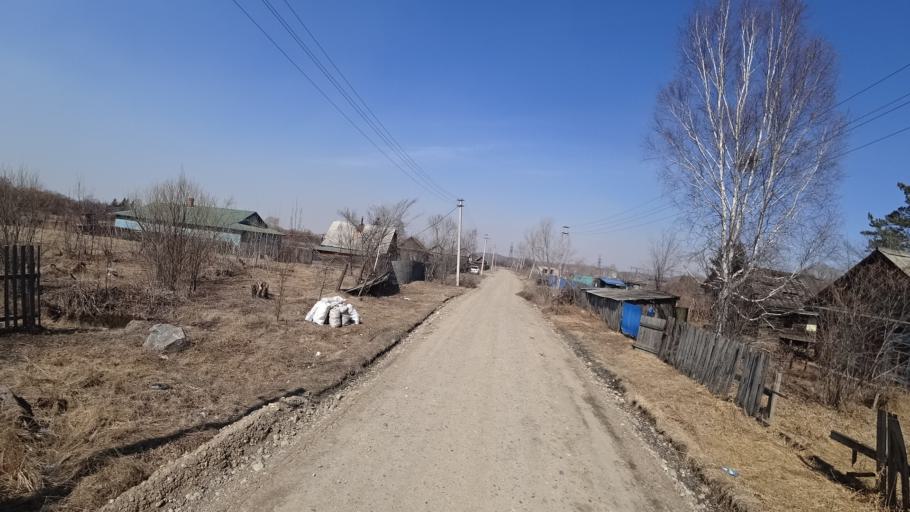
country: RU
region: Amur
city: Novobureyskiy
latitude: 49.7898
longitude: 129.8534
